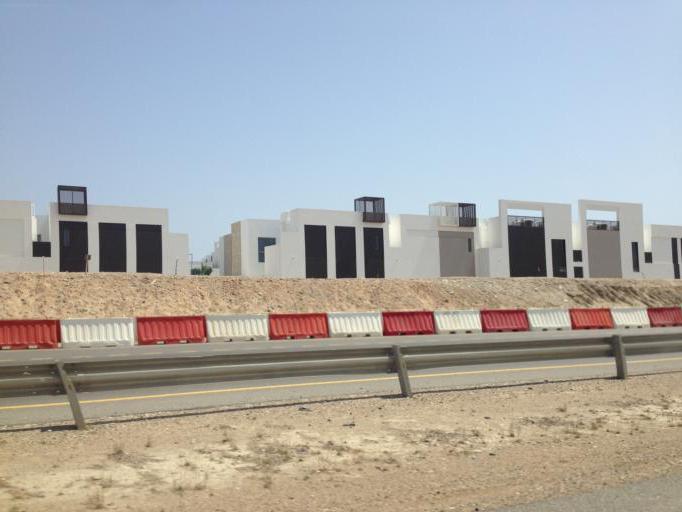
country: OM
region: Muhafazat Masqat
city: As Sib al Jadidah
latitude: 23.6182
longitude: 58.2796
